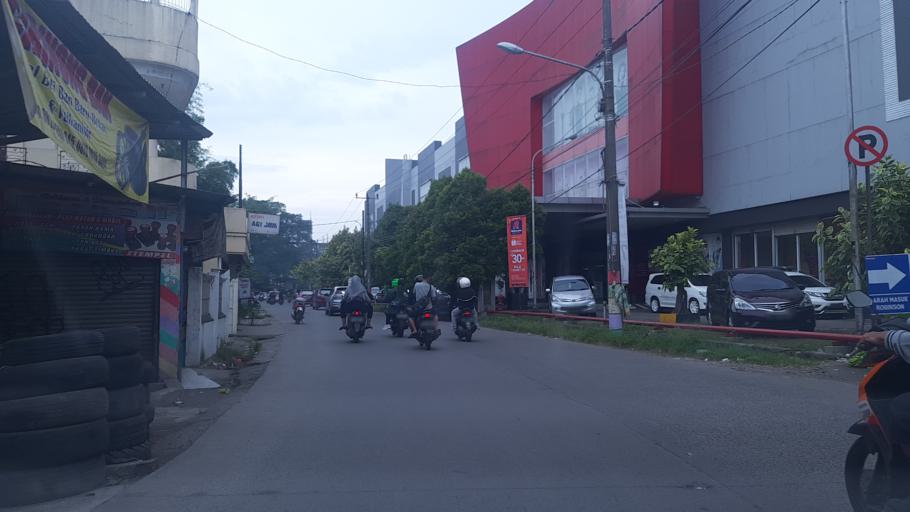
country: ID
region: West Java
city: Cibinong
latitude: -6.4685
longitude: 106.8539
